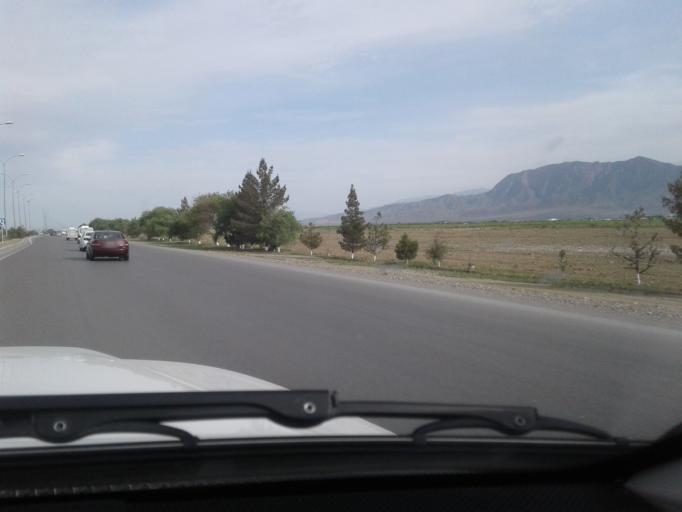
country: TM
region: Ahal
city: Abadan
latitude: 38.1259
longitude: 58.0323
